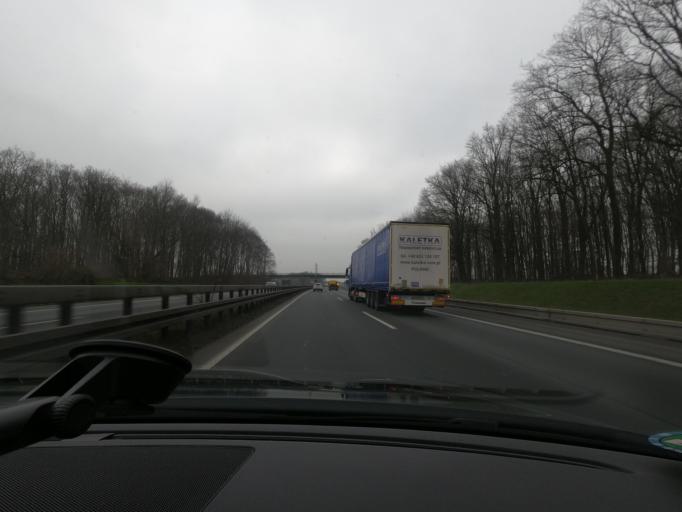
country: DE
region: North Rhine-Westphalia
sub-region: Regierungsbezirk Dusseldorf
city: Viersen
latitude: 51.2278
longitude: 6.3633
